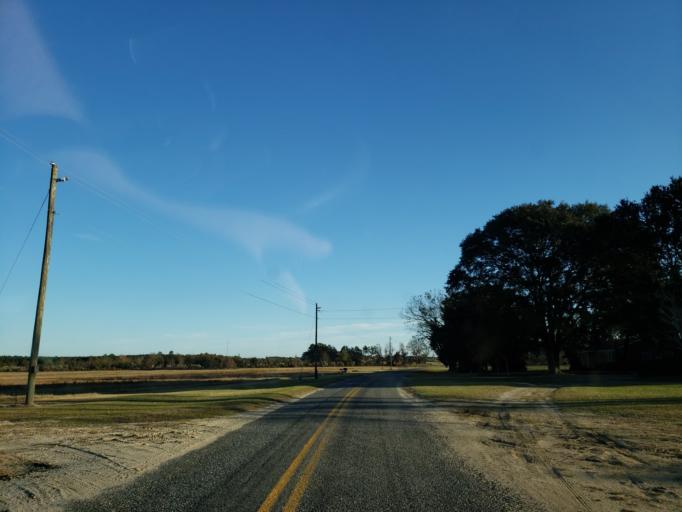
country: US
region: Georgia
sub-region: Dooly County
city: Unadilla
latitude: 32.1960
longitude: -83.7857
